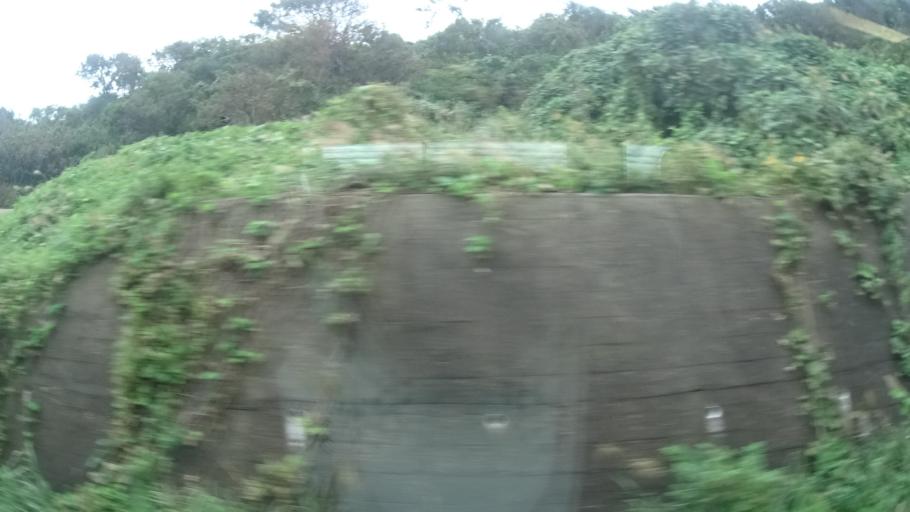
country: JP
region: Yamagata
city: Tsuruoka
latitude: 38.5497
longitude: 139.5508
